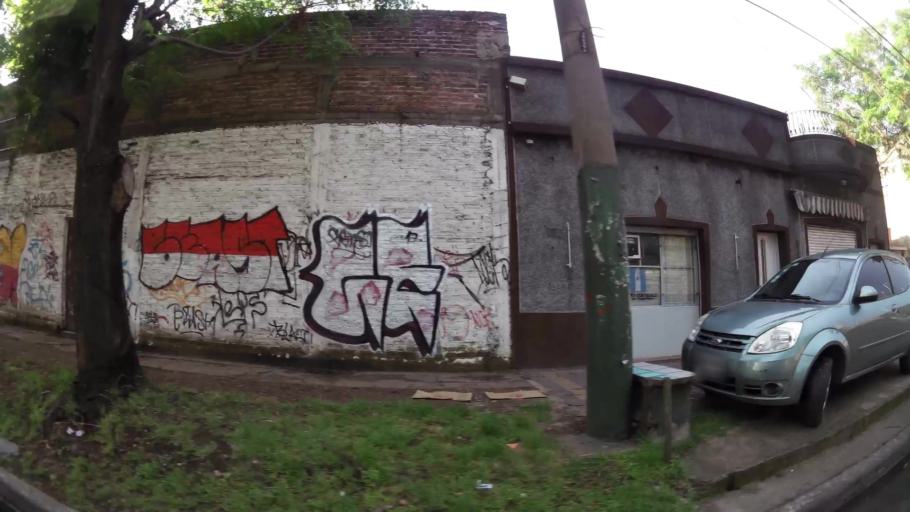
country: AR
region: Buenos Aires
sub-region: Partido de Lomas de Zamora
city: Lomas de Zamora
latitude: -34.7435
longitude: -58.3523
